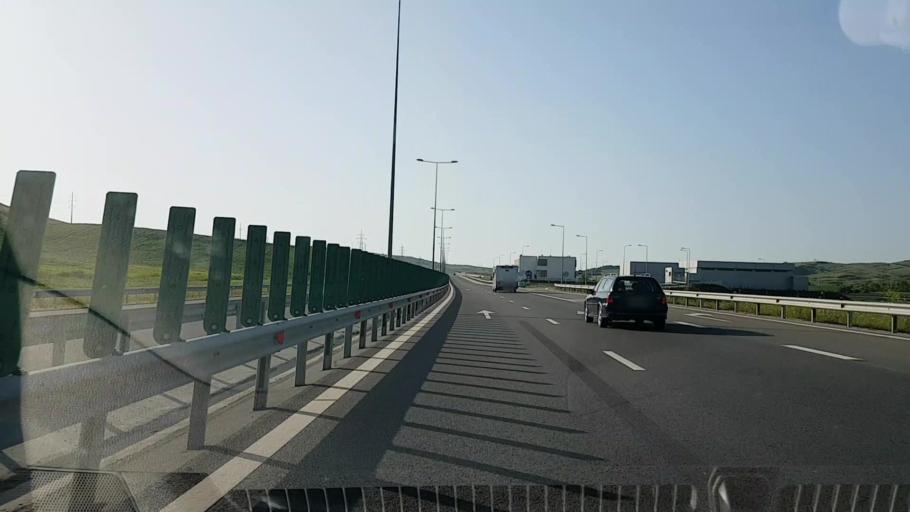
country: RO
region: Alba
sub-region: Comuna Unirea
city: Unirea
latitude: 46.4489
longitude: 23.7949
